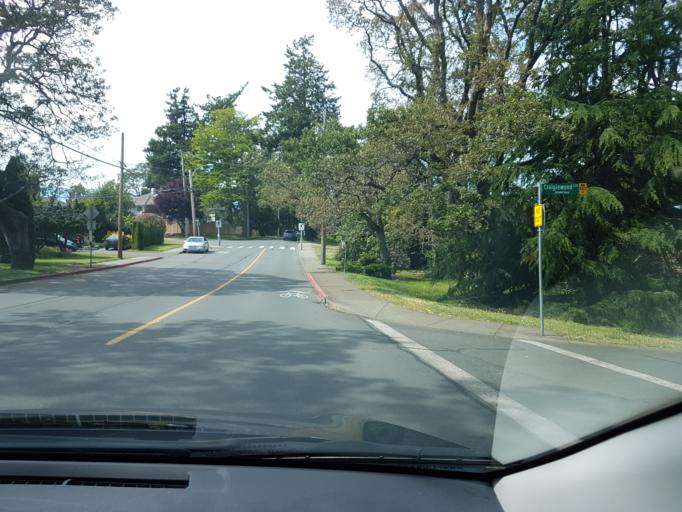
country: CA
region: British Columbia
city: Oak Bay
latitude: 48.4766
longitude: -123.3368
